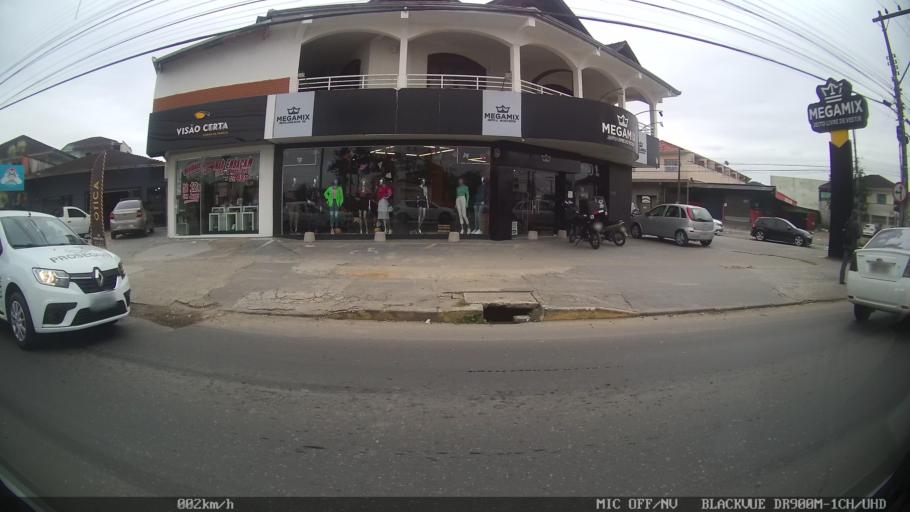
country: BR
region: Santa Catarina
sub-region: Joinville
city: Joinville
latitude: -26.2745
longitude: -48.8115
